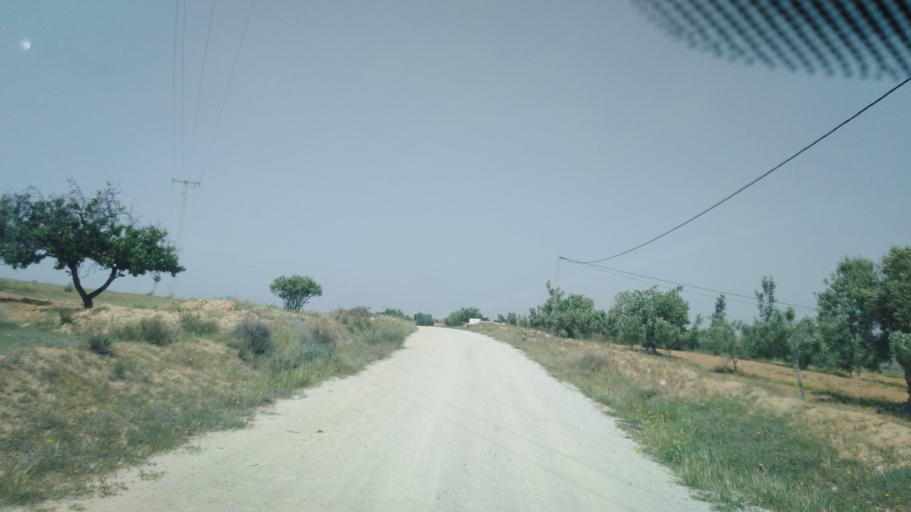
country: TN
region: Safaqis
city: Sfax
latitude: 34.7516
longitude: 10.5633
